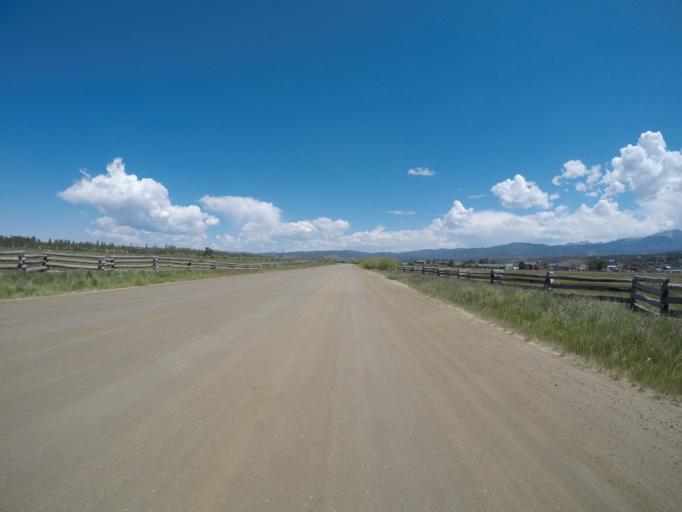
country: US
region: Colorado
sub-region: Grand County
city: Fraser
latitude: 39.9426
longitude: -105.8230
